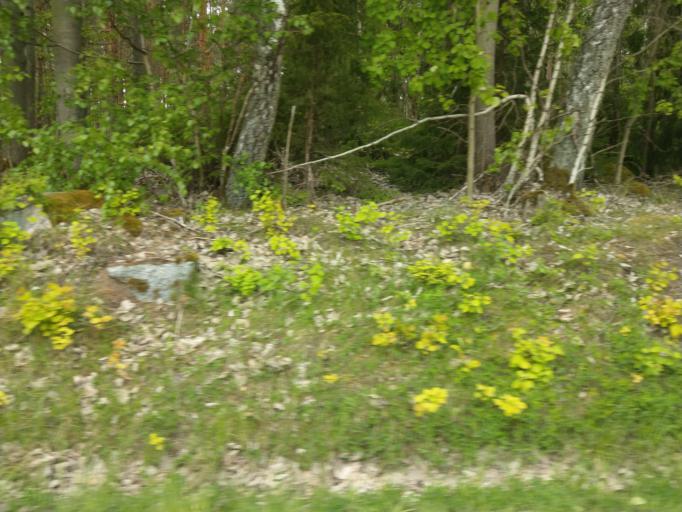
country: SE
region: Stockholm
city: Stenhamra
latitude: 59.4108
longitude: 17.6213
